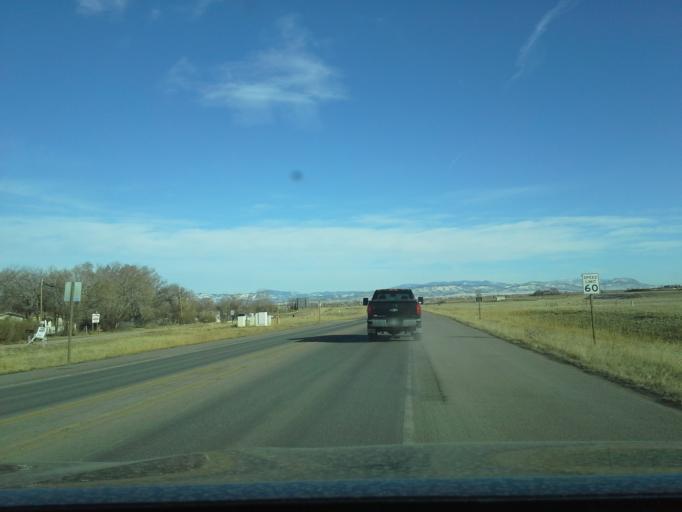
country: US
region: Montana
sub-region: Lewis and Clark County
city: Helena
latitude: 46.6165
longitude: -111.9886
